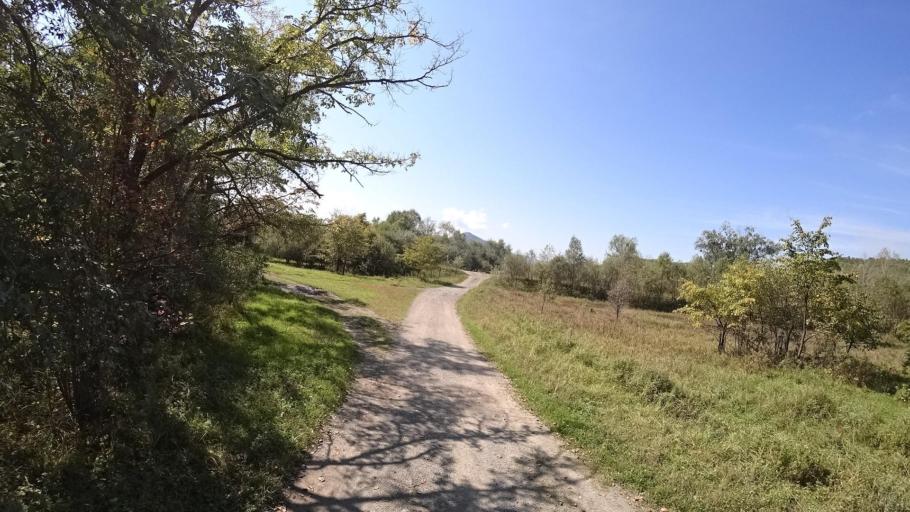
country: RU
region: Jewish Autonomous Oblast
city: Londoko
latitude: 49.0035
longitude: 131.9391
